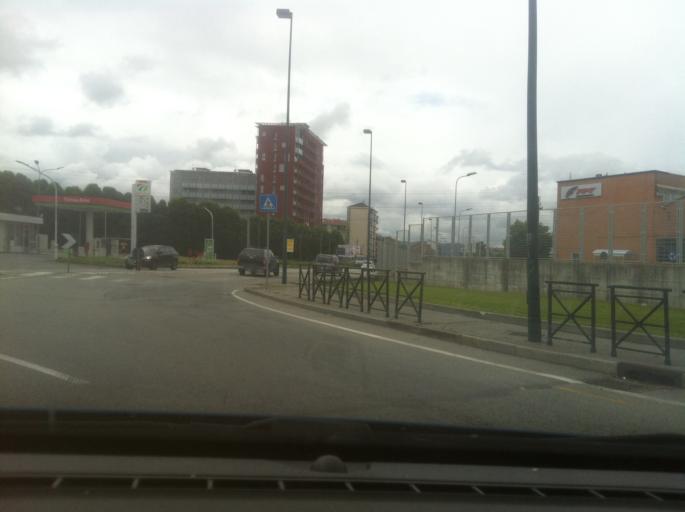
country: IT
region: Piedmont
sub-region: Provincia di Torino
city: San Mauro Torinese
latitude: 45.1099
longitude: 7.7287
